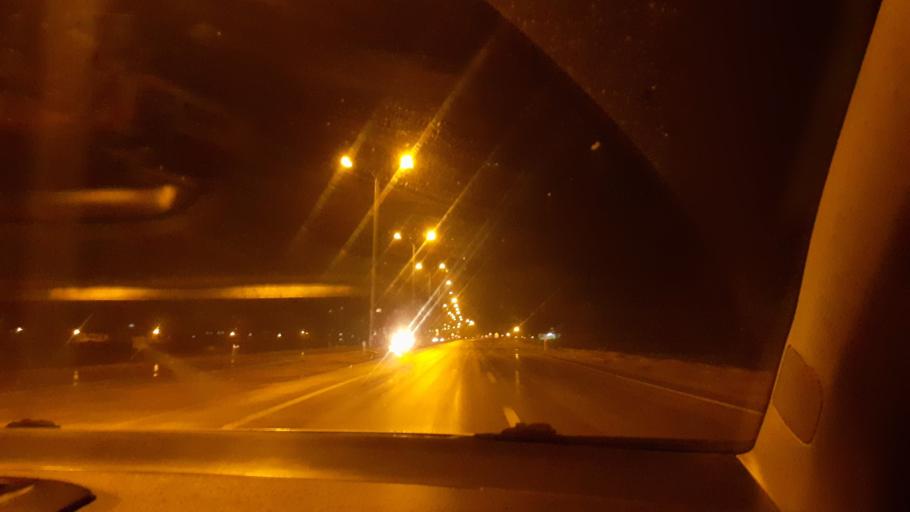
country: TR
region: Hatay
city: Aktepe
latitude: 36.7187
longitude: 36.5126
